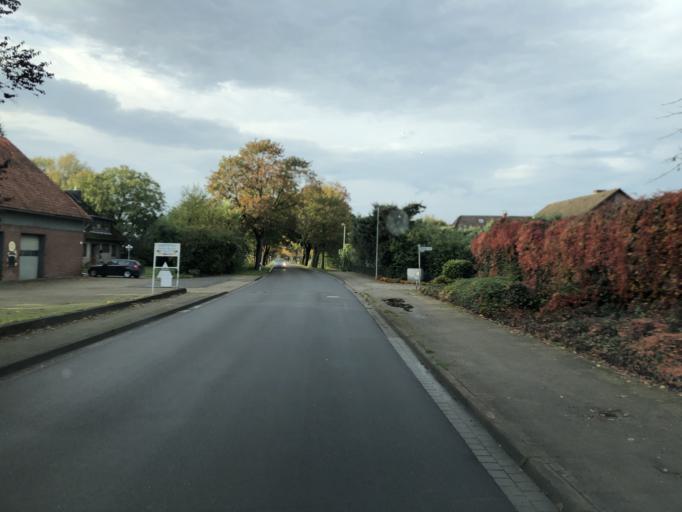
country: DE
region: Lower Saxony
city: Neu Wulmstorf
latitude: 53.4446
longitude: 9.8034
